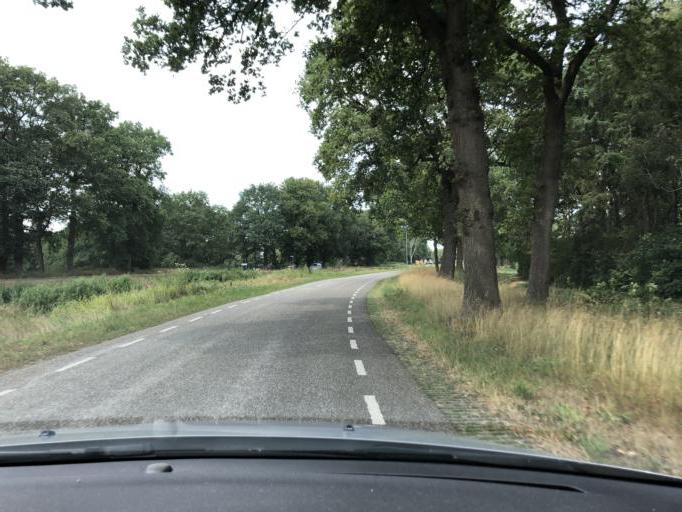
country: NL
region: Drenthe
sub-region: Gemeente Borger-Odoorn
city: Borger
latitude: 52.8489
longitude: 6.6642
